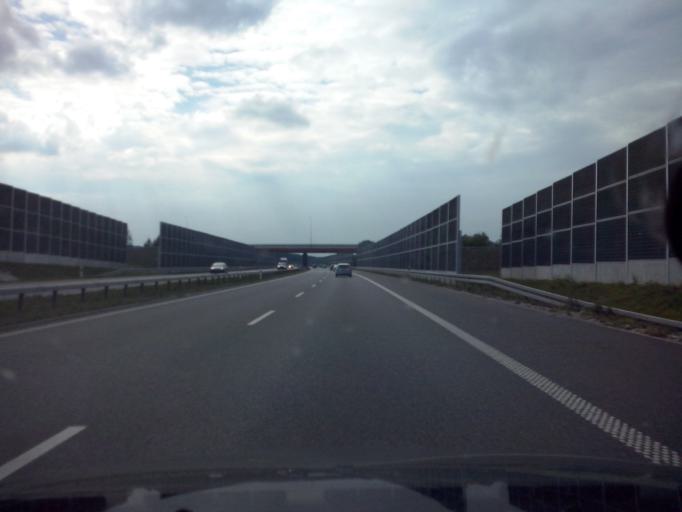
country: PL
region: Lesser Poland Voivodeship
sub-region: Powiat brzeski
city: Maszkienice
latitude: 50.0041
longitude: 20.6667
